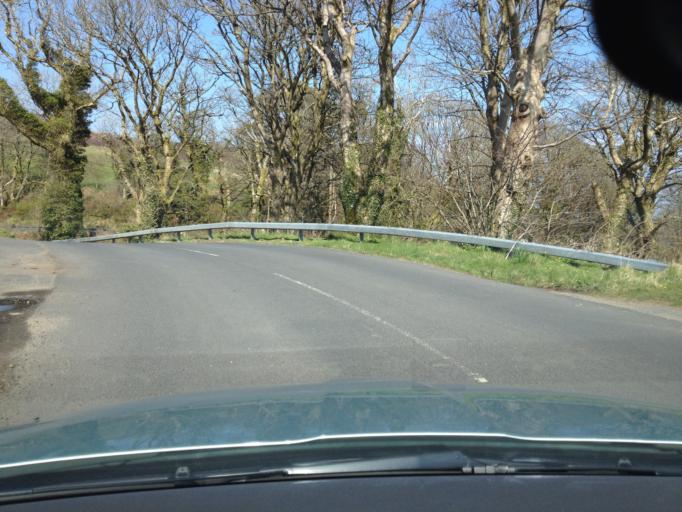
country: GB
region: Scotland
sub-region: North Ayrshire
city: Lamlash
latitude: 55.4572
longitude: -5.0893
